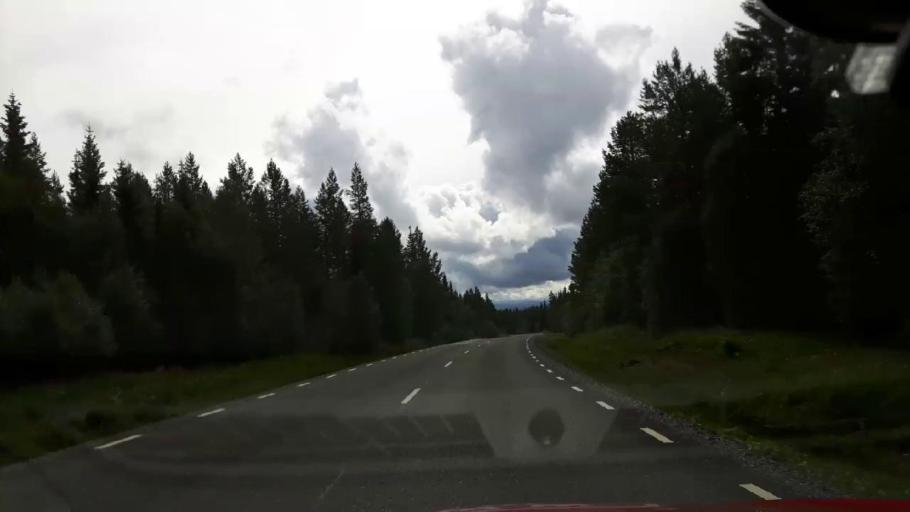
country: NO
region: Nord-Trondelag
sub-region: Lierne
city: Sandvika
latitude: 64.6227
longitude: 14.1222
